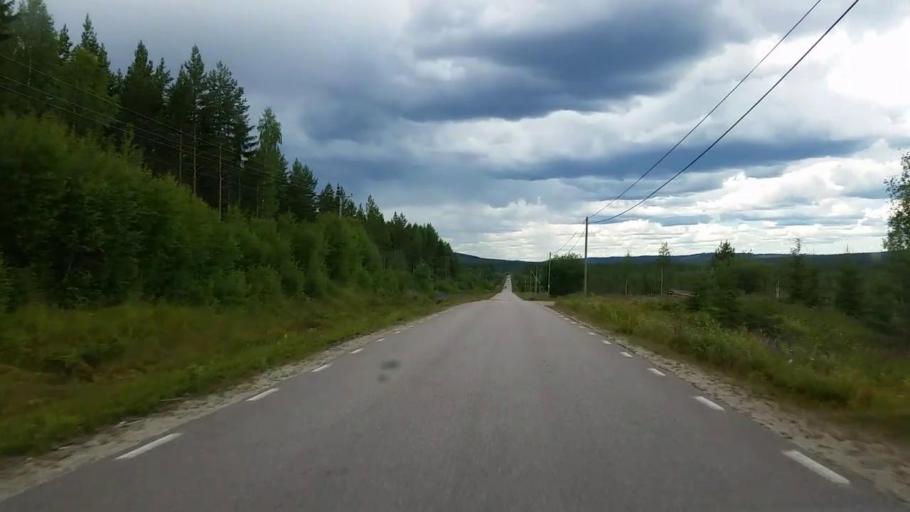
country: SE
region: Gaevleborg
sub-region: Ovanakers Kommun
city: Edsbyn
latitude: 61.4371
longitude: 15.8942
